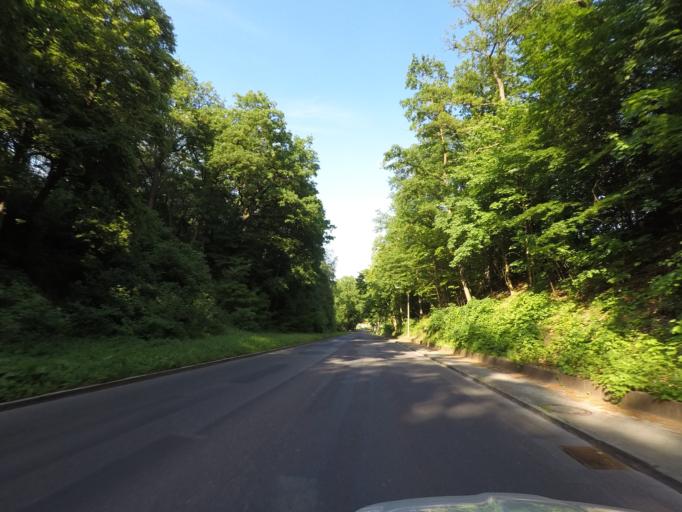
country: DE
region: Brandenburg
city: Bad Freienwalde
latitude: 52.7776
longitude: 14.0160
